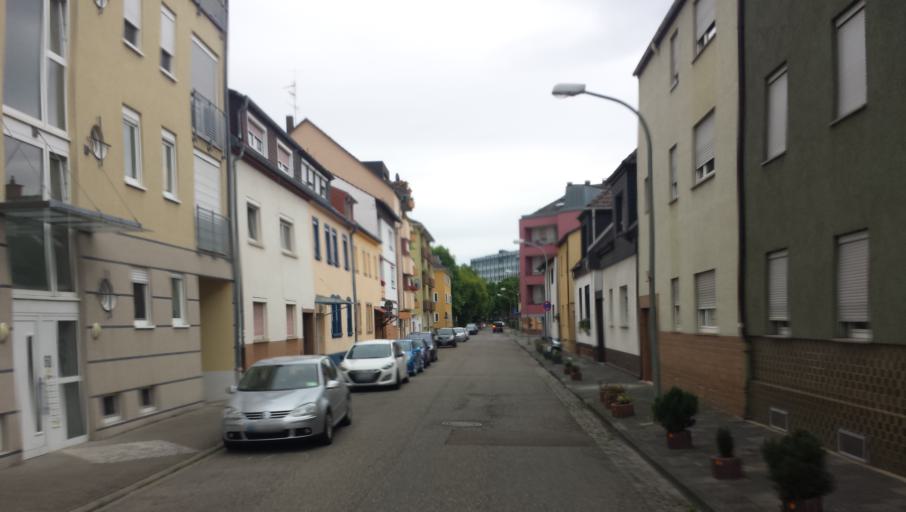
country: DE
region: Rheinland-Pfalz
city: Ludwigshafen am Rhein
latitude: 49.4987
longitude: 8.4210
